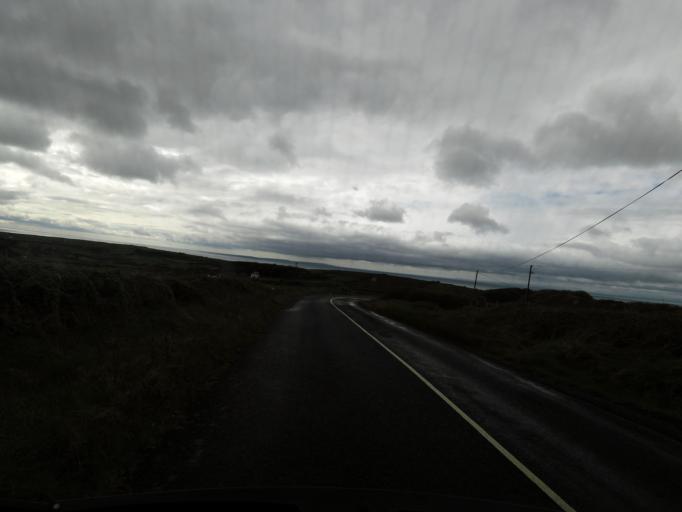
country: IE
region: Connaught
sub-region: County Galway
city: Bearna
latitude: 53.0432
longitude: -9.3374
